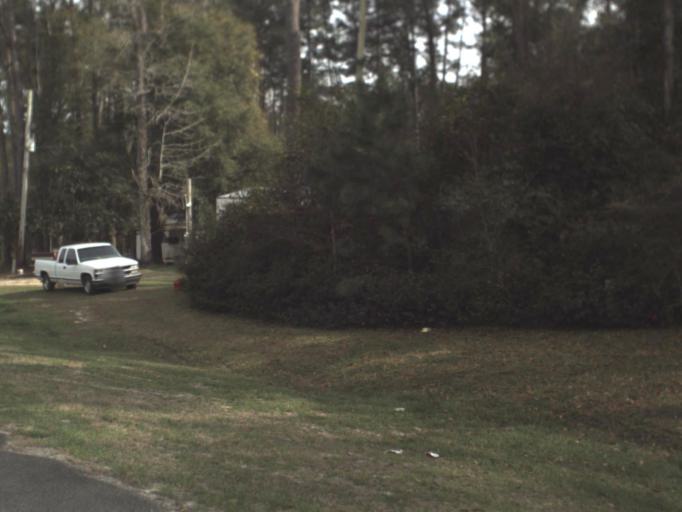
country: US
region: Florida
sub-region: Jefferson County
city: Monticello
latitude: 30.5451
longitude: -83.8501
